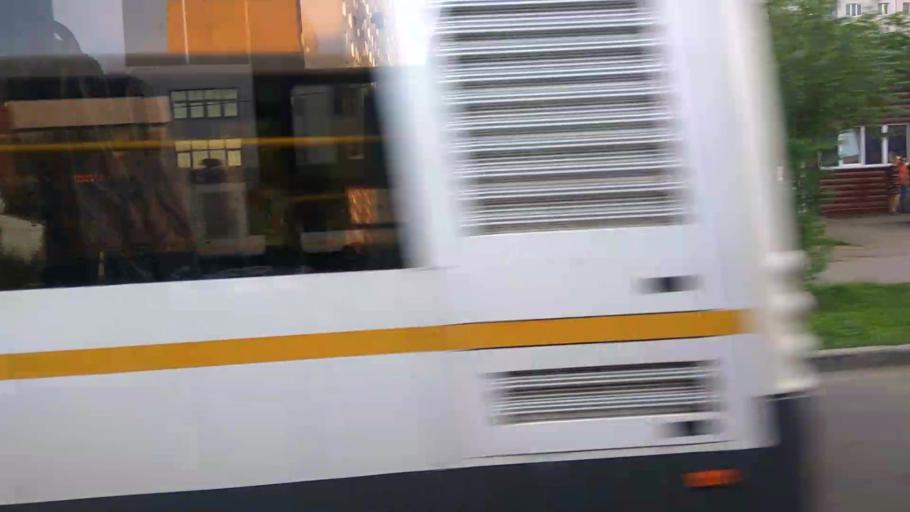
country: RU
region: Moskovskaya
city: Korolev
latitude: 55.9075
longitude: 37.8662
